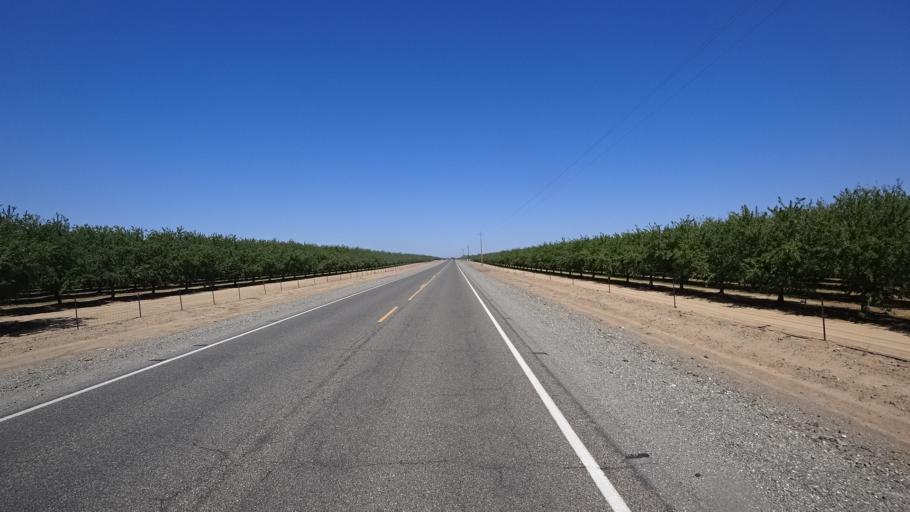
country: US
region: California
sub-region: Glenn County
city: Orland
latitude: 39.6699
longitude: -122.1970
